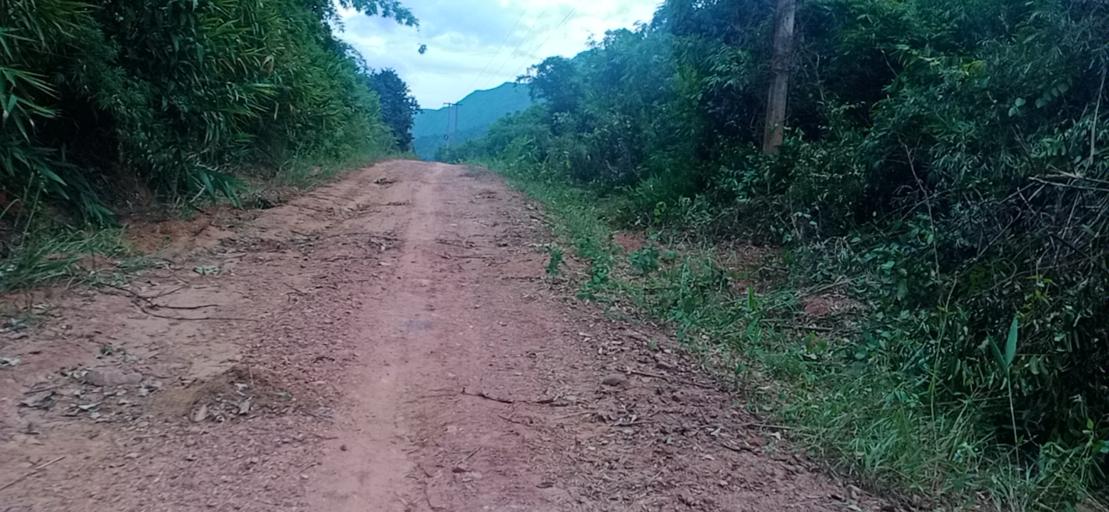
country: TH
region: Changwat Bueng Kan
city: Pak Khat
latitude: 18.5602
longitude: 103.2268
